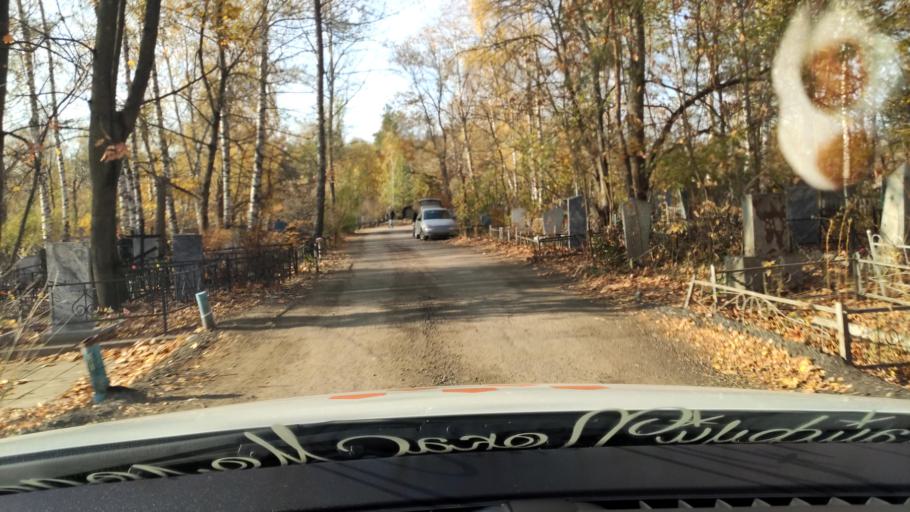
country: RU
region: Voronezj
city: Pridonskoy
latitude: 51.6706
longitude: 39.1079
